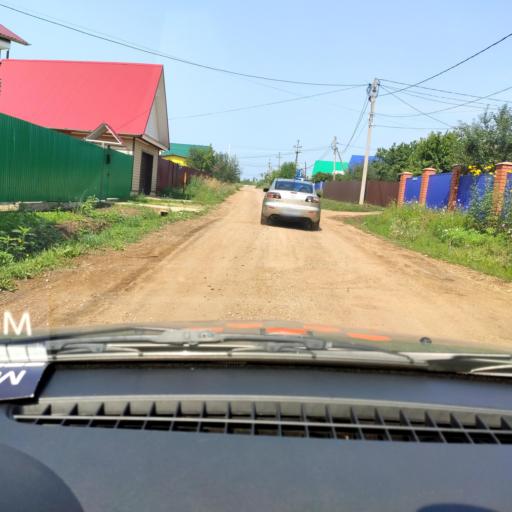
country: RU
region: Bashkortostan
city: Iglino
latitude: 54.8407
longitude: 56.4001
